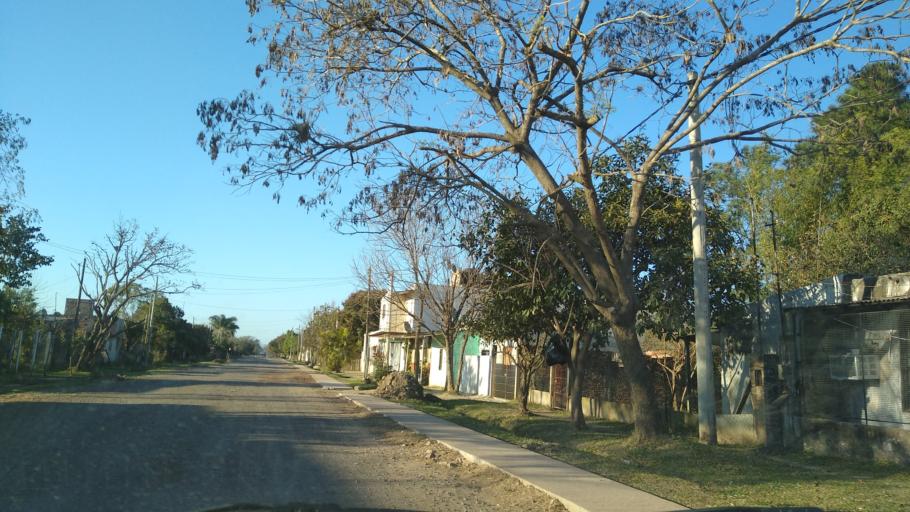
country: AR
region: Chaco
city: Barranqueras
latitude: -27.4656
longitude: -58.9504
